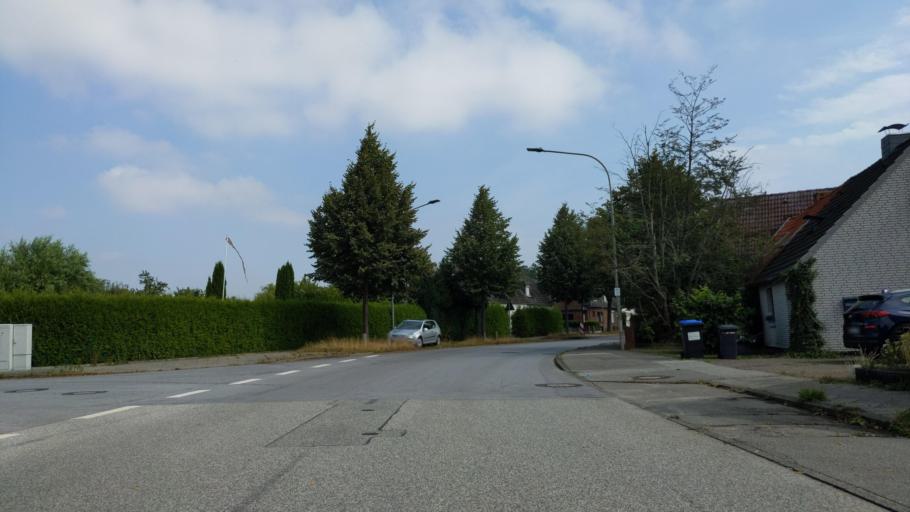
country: DE
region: Schleswig-Holstein
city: Stockelsdorf
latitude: 53.8721
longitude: 10.6247
